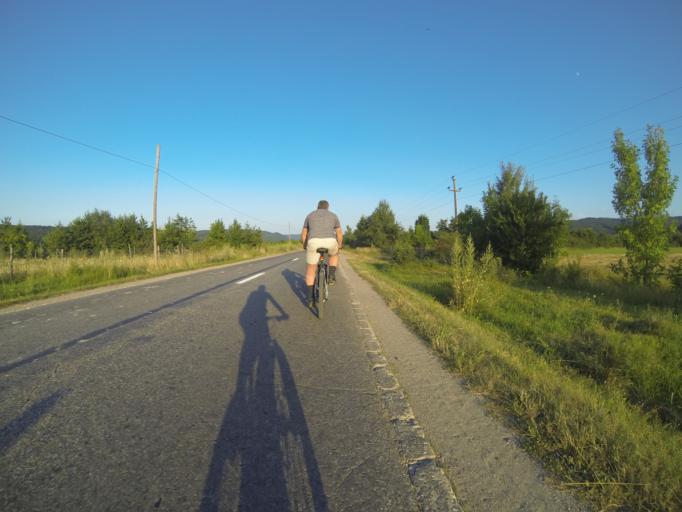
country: RO
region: Brasov
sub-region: Comuna Sinca Veche
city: Sinca Veche
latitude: 45.7480
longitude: 25.1888
